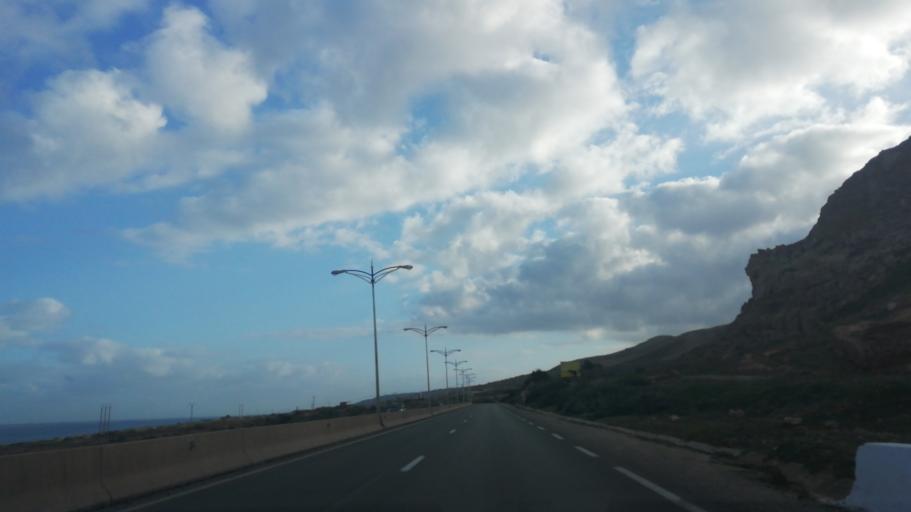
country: DZ
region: Mostaganem
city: Mostaganem
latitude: 36.0558
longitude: 0.1608
